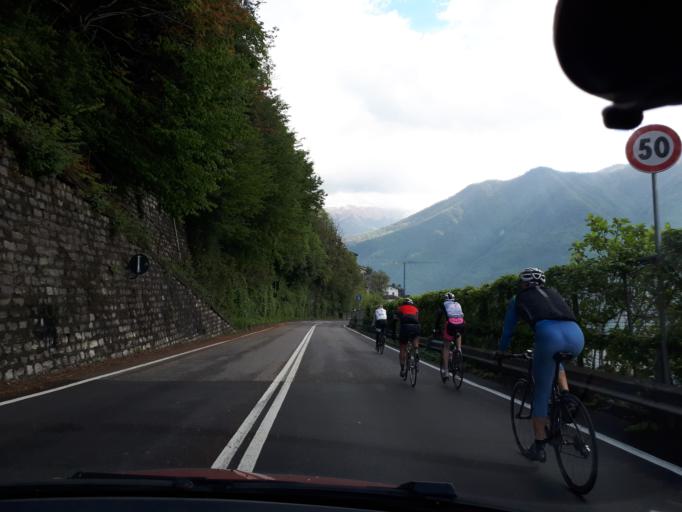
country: IT
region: Lombardy
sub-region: Provincia di Como
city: Carate Urio
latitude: 45.8731
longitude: 9.1236
